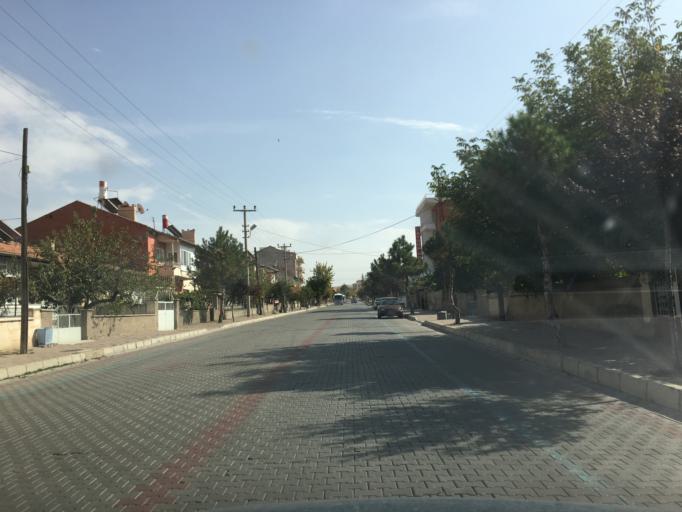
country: TR
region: Nevsehir
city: Avanos
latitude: 38.7114
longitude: 34.8465
